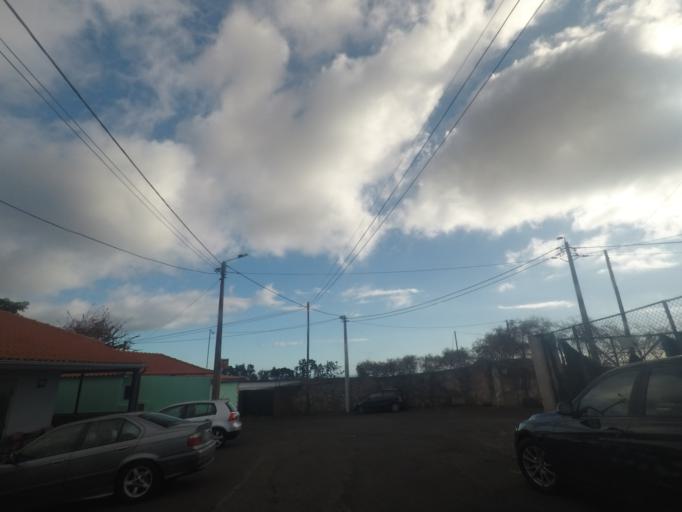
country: PT
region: Madeira
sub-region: Santa Cruz
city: Camacha
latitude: 32.6627
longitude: -16.8655
